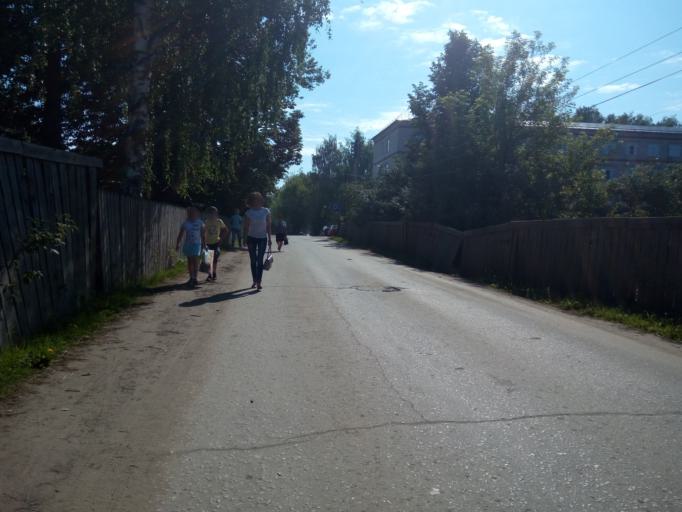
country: RU
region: Nizjnij Novgorod
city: Voskresenskoye
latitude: 56.8319
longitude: 45.4368
